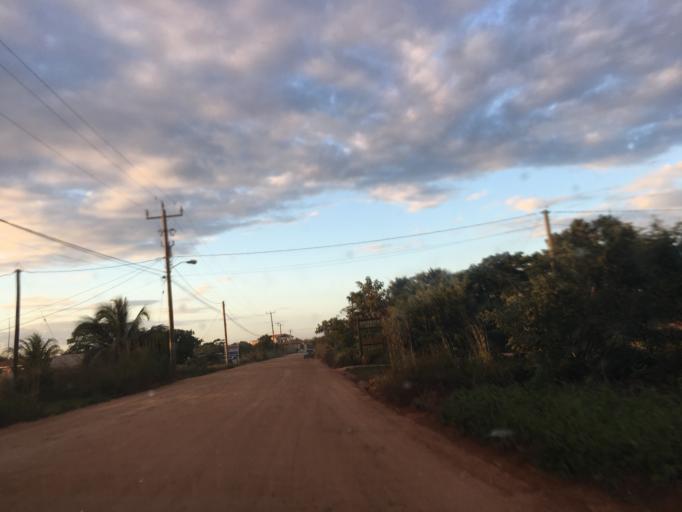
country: BZ
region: Stann Creek
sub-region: Dangriga
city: Dangriga
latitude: 16.8477
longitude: -88.2787
